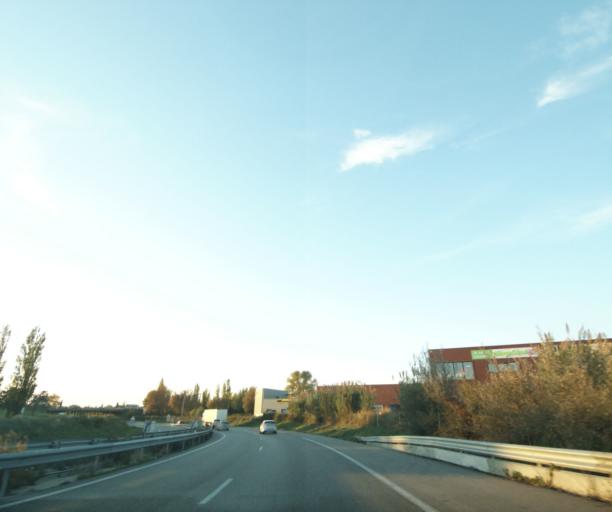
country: FR
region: Provence-Alpes-Cote d'Azur
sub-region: Departement des Bouches-du-Rhone
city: Pelissanne
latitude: 43.6279
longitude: 5.1301
